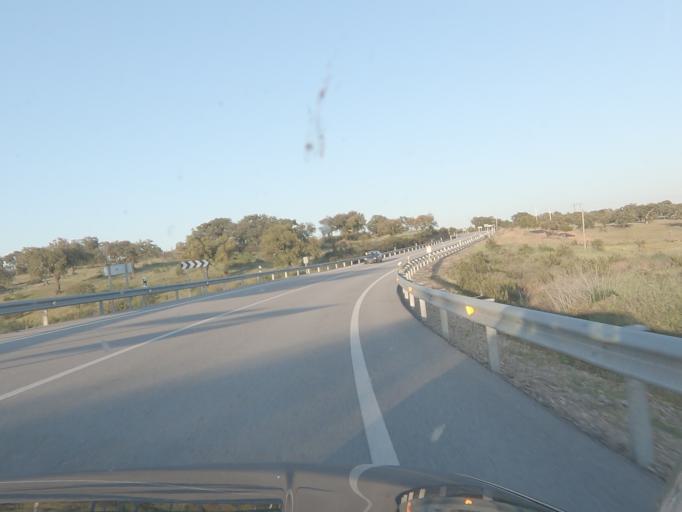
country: ES
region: Extremadura
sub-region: Provincia de Caceres
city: Carbajo
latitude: 39.5049
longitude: -7.1604
